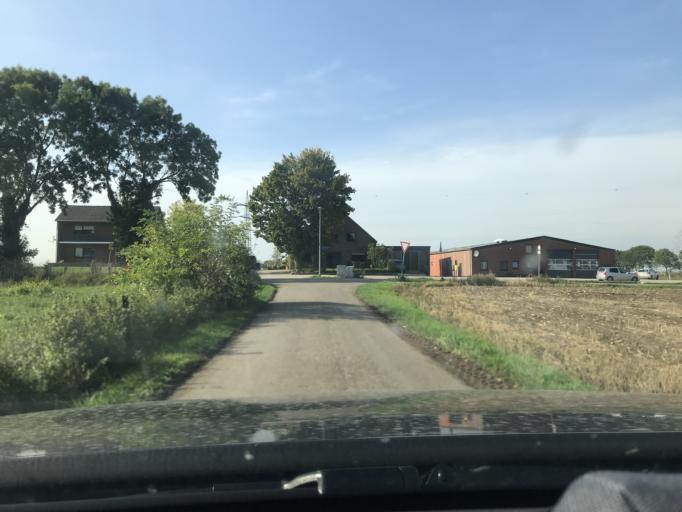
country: DE
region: North Rhine-Westphalia
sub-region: Regierungsbezirk Dusseldorf
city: Emmerich
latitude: 51.8189
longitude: 6.2071
